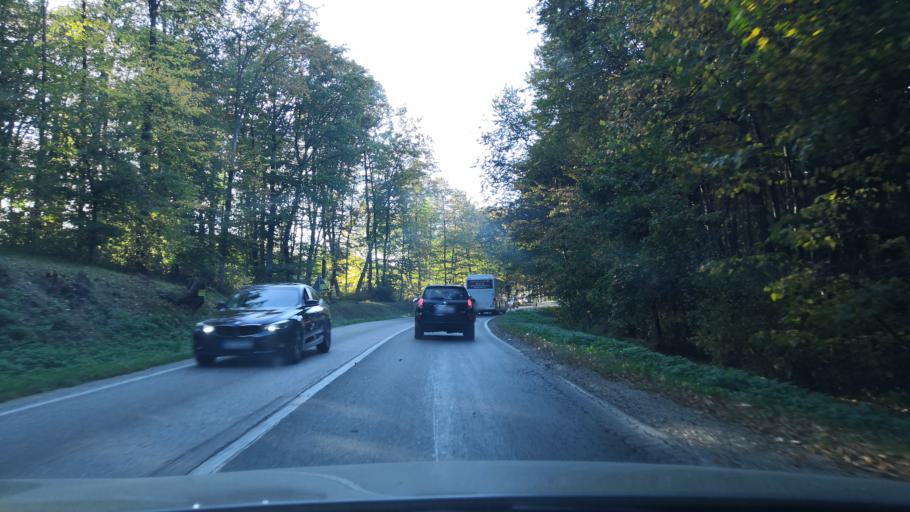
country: RS
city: Vrdnik
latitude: 45.1460
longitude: 19.8334
